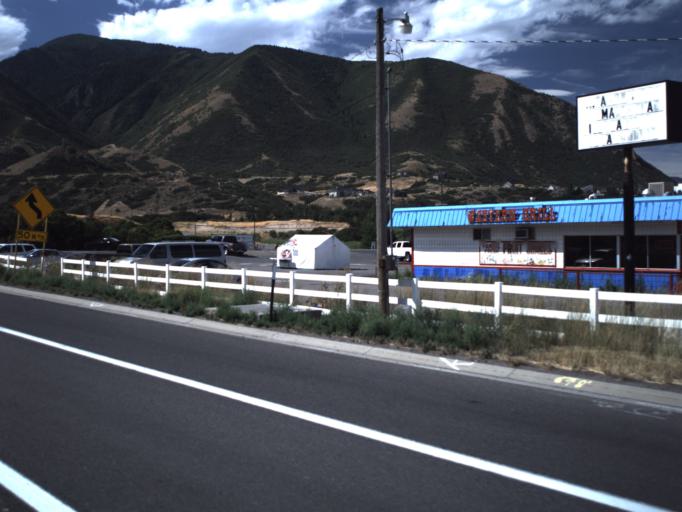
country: US
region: Utah
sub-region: Utah County
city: Mapleton
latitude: 40.0869
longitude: -111.5931
